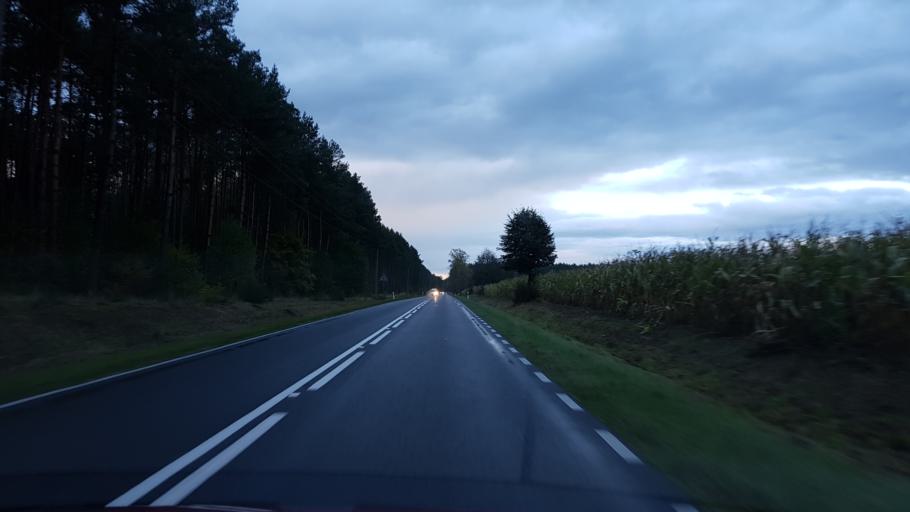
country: PL
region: Greater Poland Voivodeship
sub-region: Powiat zlotowski
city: Tarnowka
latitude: 53.2429
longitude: 16.8880
